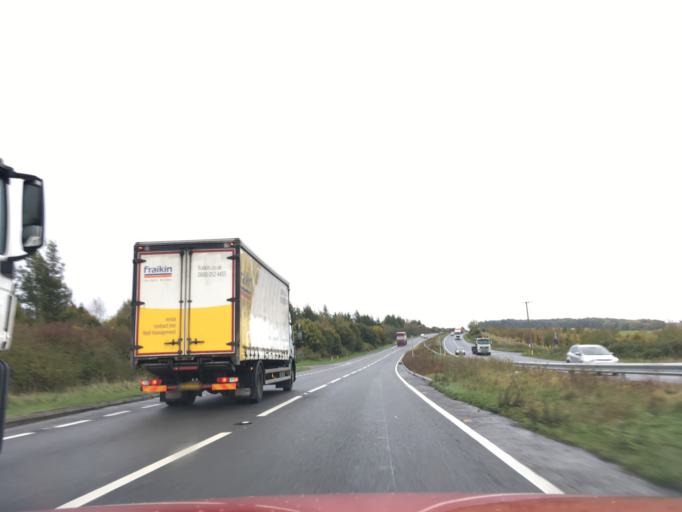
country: GB
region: England
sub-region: Hampshire
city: Overton
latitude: 51.2003
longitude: -1.3373
